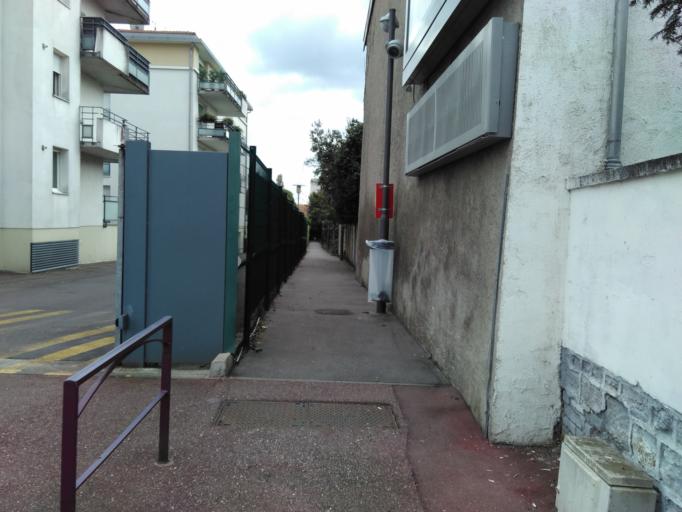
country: FR
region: Lorraine
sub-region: Departement de Meurthe-et-Moselle
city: Essey-les-Nancy
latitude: 48.7051
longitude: 6.2253
